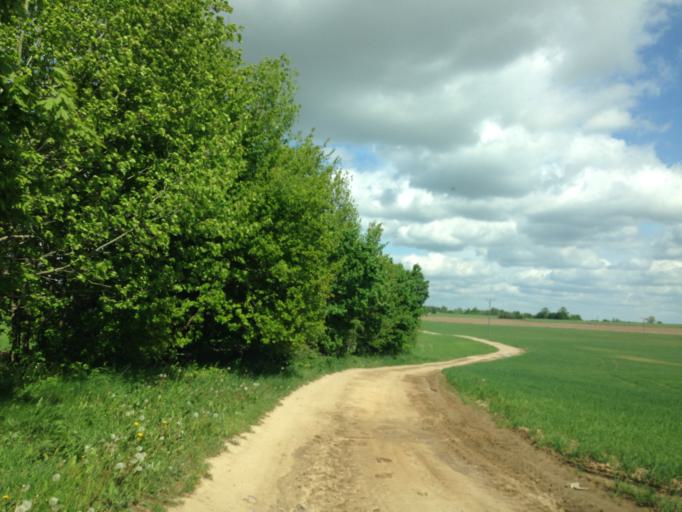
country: PL
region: Warmian-Masurian Voivodeship
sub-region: Powiat nidzicki
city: Kozlowo
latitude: 53.3962
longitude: 20.1960
